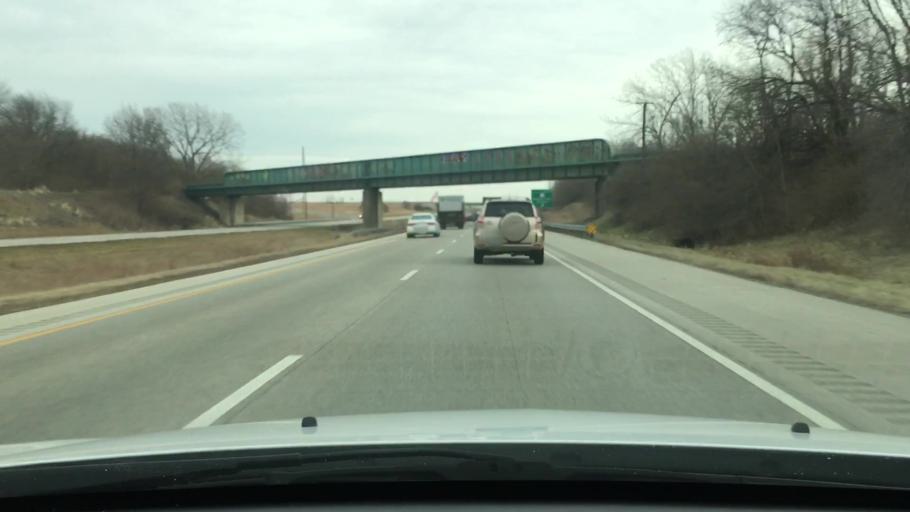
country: US
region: Illinois
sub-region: Sangamon County
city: Jerome
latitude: 39.7450
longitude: -89.7144
